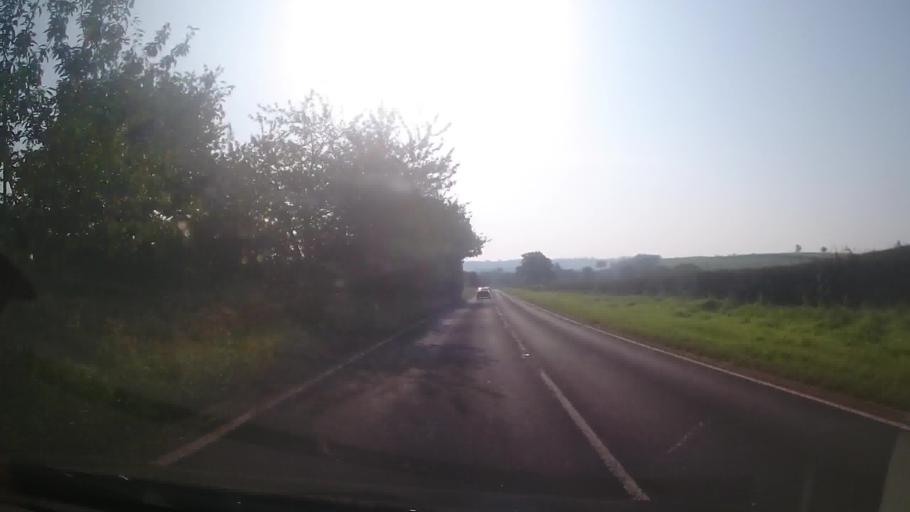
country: GB
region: England
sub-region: Shropshire
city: Much Wenlock
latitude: 52.5638
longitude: -2.5267
